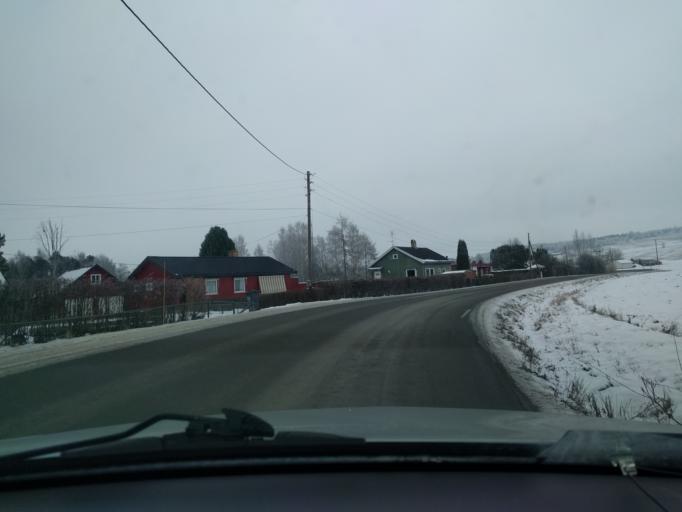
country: NO
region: Hedmark
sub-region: Hamar
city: Hamar
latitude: 60.7874
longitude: 11.1434
